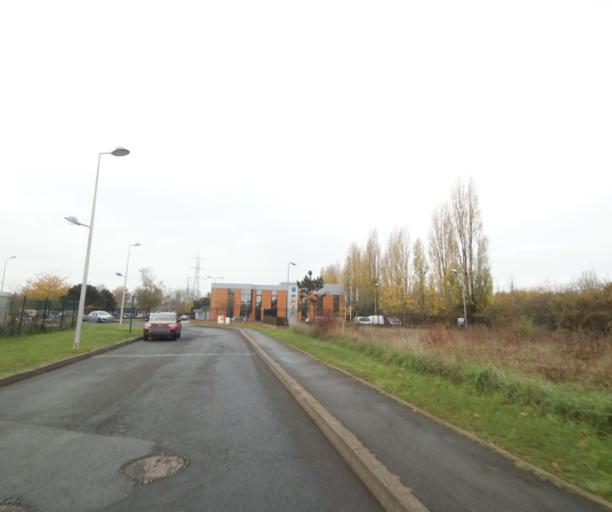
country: FR
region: Ile-de-France
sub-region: Departement de l'Essonne
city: Lisses
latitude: 48.6137
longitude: 2.4339
